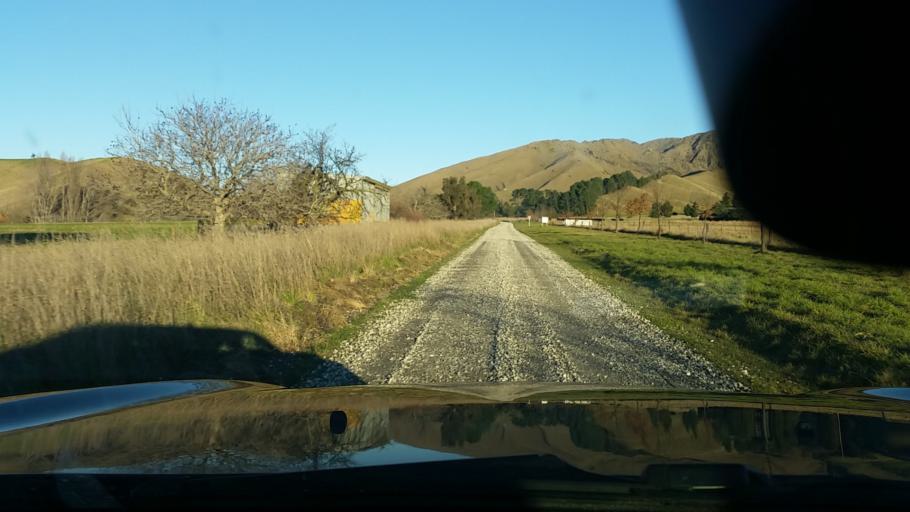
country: NZ
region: Marlborough
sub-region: Marlborough District
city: Blenheim
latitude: -41.7328
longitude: 174.0377
